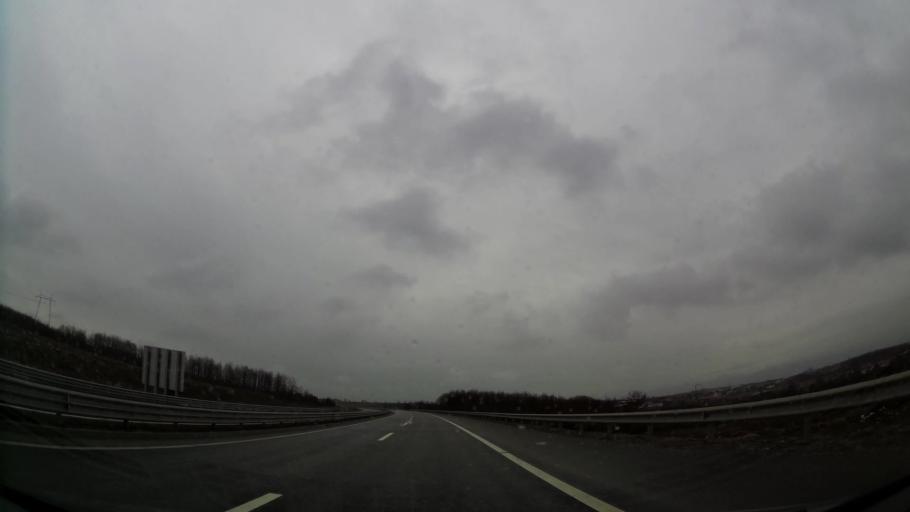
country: XK
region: Ferizaj
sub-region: Komuna e Ferizajt
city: Ferizaj
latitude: 42.3625
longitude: 21.2023
